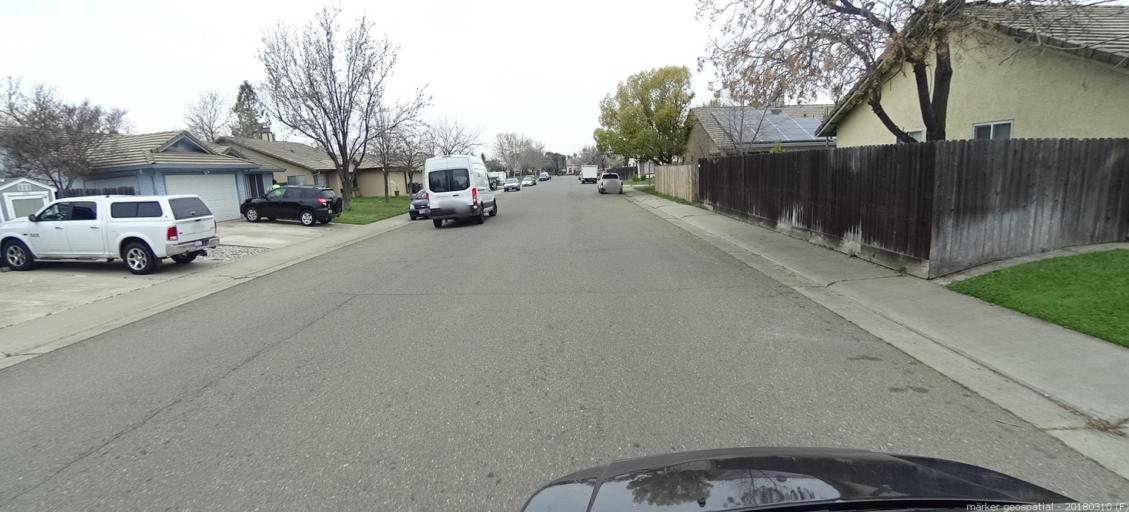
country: US
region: California
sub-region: Sacramento County
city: Vineyard
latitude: 38.4678
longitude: -121.3648
